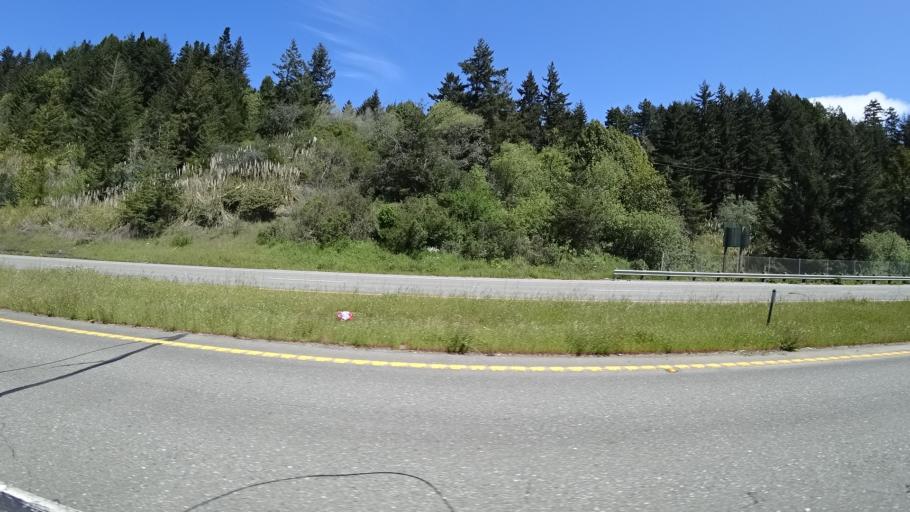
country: US
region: California
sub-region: Humboldt County
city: Arcata
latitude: 40.9083
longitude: -124.0461
